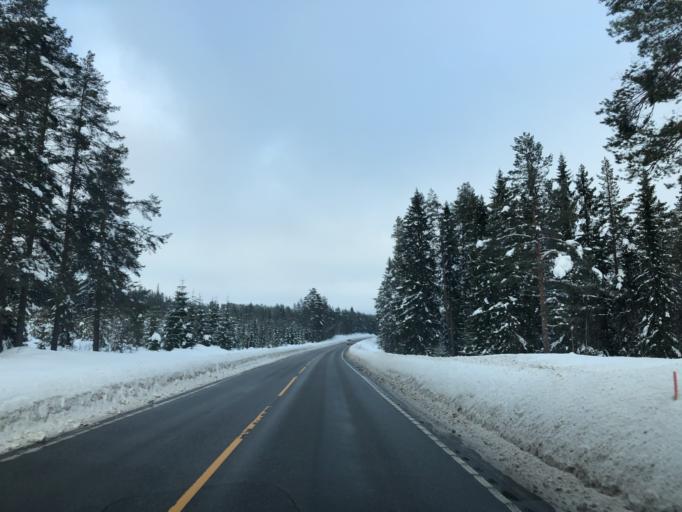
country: NO
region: Hedmark
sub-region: Trysil
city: Innbygda
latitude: 61.2234
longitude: 12.2452
